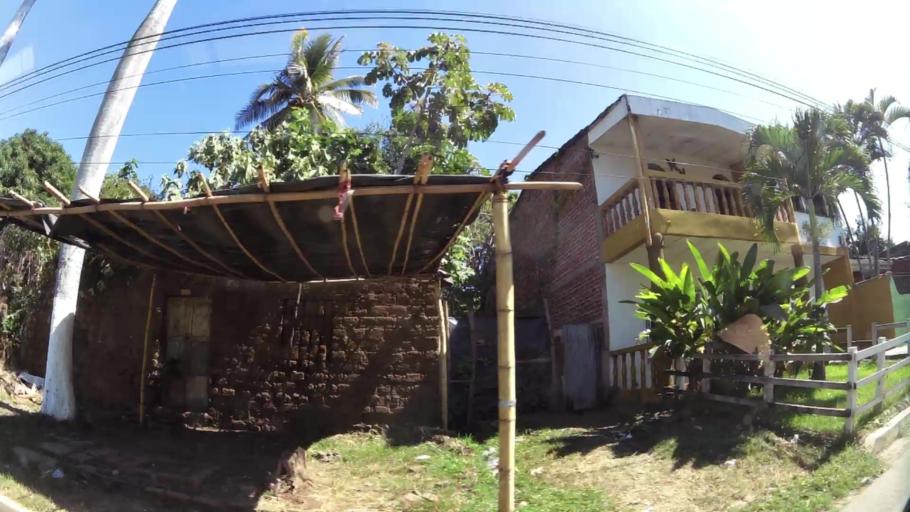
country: SV
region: Ahuachapan
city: Atiquizaya
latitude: 13.9711
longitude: -89.7581
